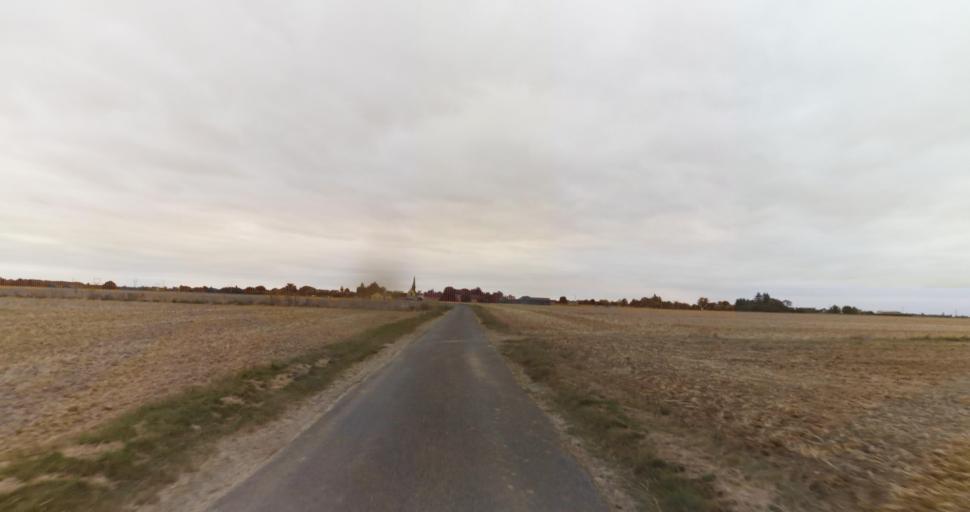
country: FR
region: Haute-Normandie
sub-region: Departement de l'Eure
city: Marcilly-sur-Eure
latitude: 48.8655
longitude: 1.2555
